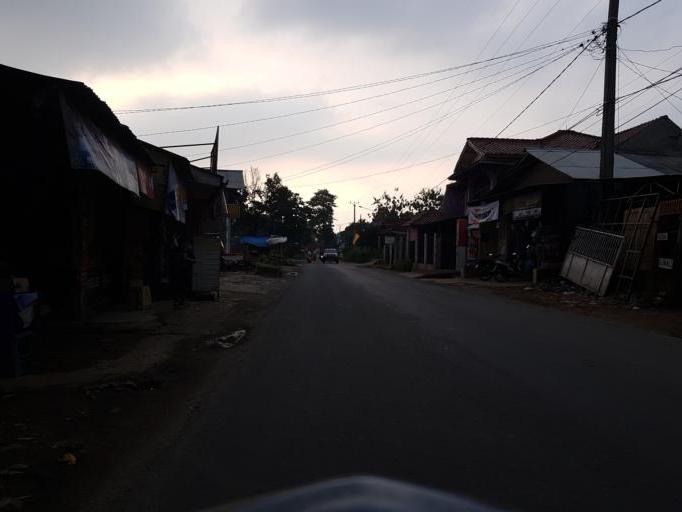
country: ID
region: West Java
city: Parung
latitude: -6.4739
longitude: 106.7224
